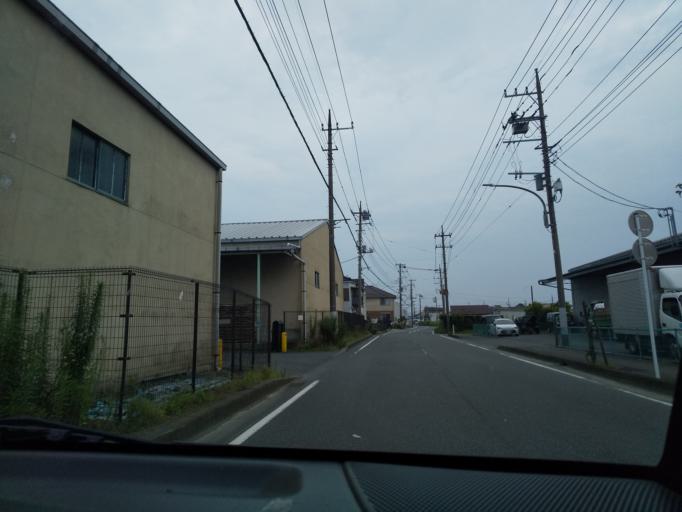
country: JP
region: Kanagawa
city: Atsugi
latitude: 35.4011
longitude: 139.3859
